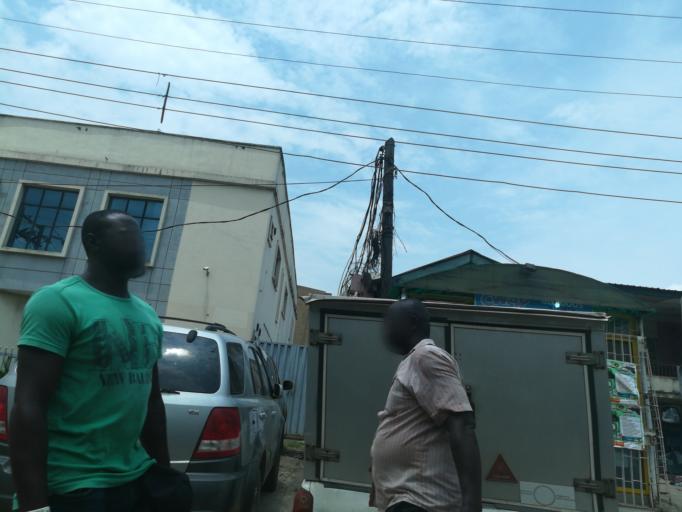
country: NG
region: Lagos
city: Oshodi
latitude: 6.5485
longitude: 3.3321
